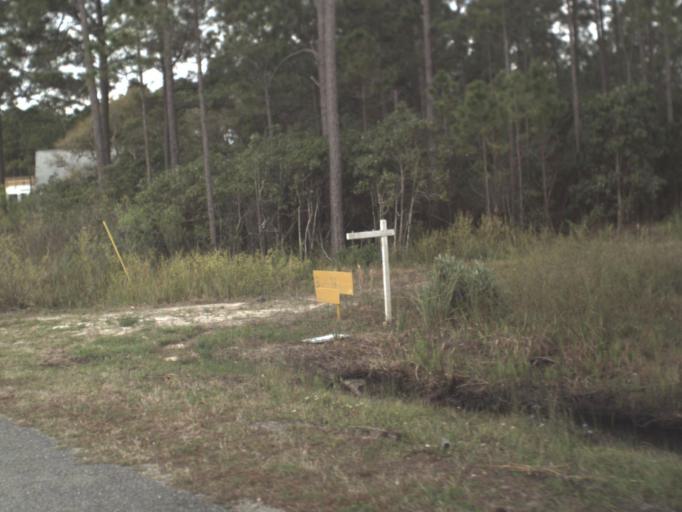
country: US
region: Florida
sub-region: Franklin County
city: Carrabelle
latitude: 29.8045
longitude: -84.7359
